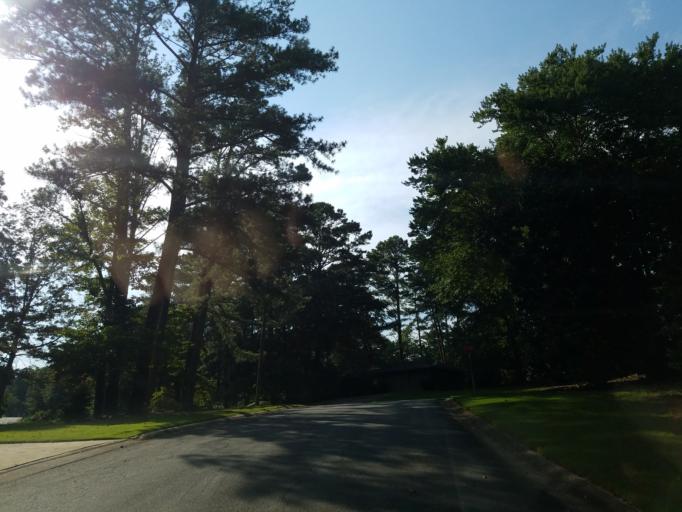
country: US
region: Georgia
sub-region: Fulton County
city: Sandy Springs
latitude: 33.9644
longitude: -84.4408
